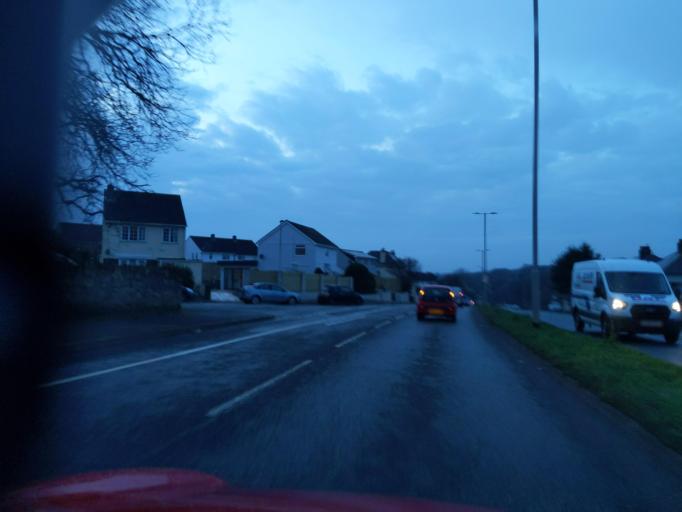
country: GB
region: England
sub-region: Plymouth
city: Plymstock
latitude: 50.3640
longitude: -4.0766
